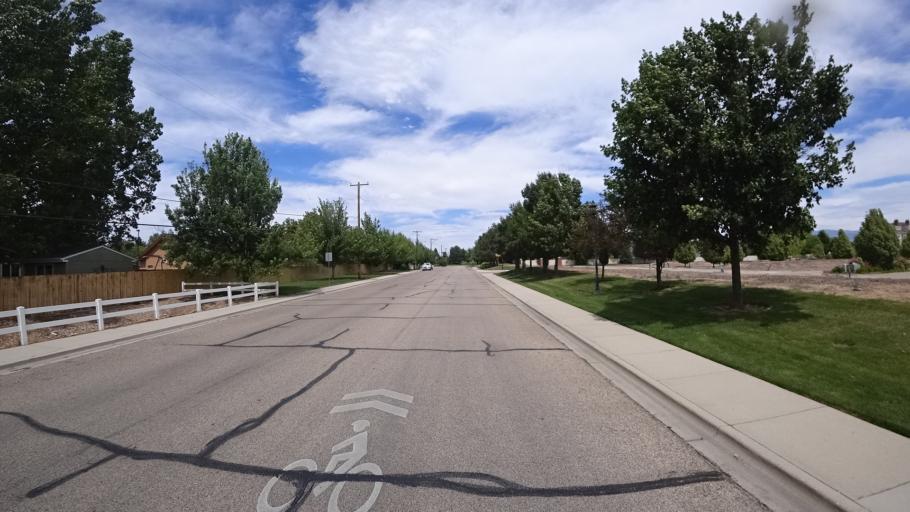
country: US
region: Idaho
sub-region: Ada County
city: Meridian
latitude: 43.6212
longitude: -116.3243
